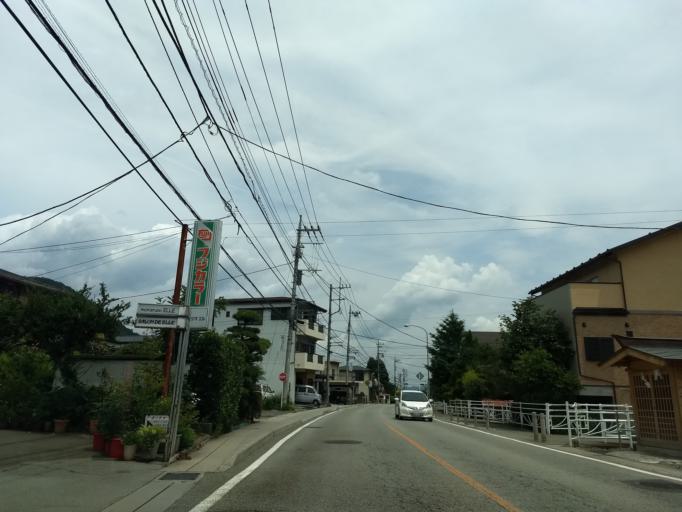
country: JP
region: Yamanashi
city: Otsuki
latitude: 35.5249
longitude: 138.8491
